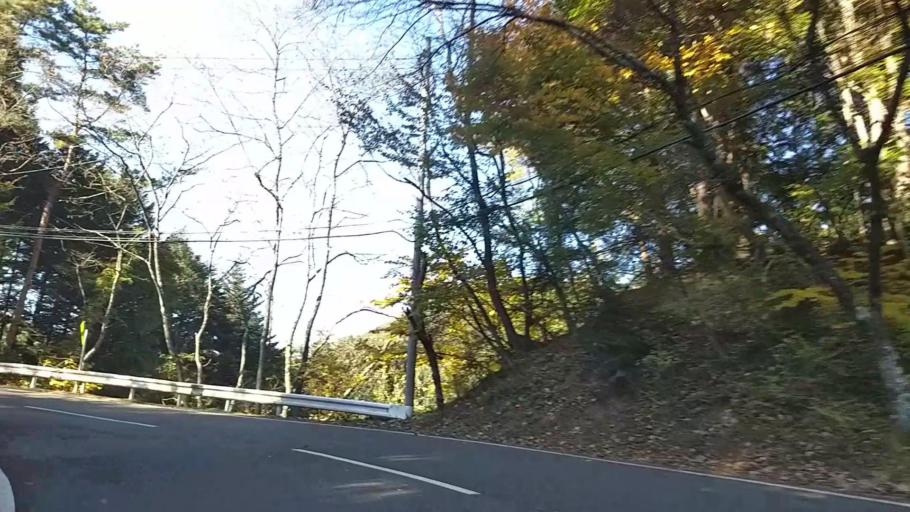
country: JP
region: Yamanashi
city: Otsuki
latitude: 35.7489
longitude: 138.9604
